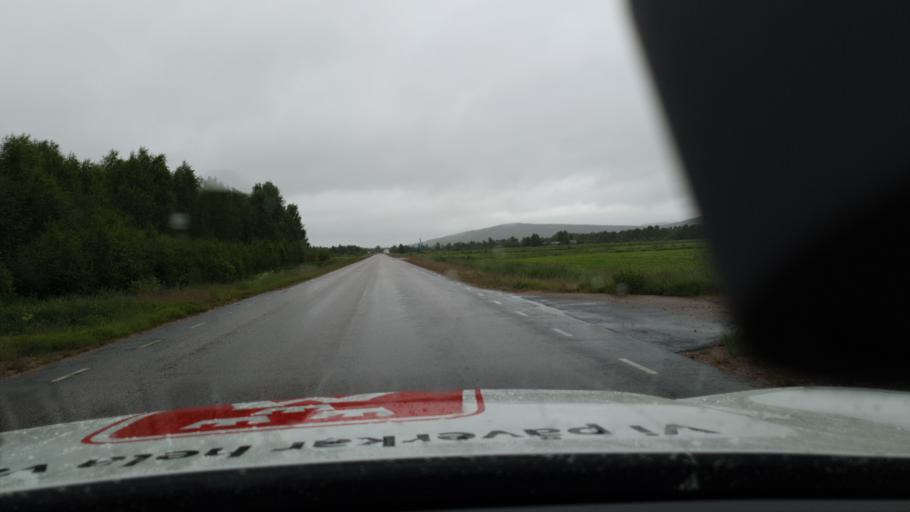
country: SE
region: Norrbotten
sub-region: Overtornea Kommun
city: OEvertornea
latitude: 66.5510
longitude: 23.8006
